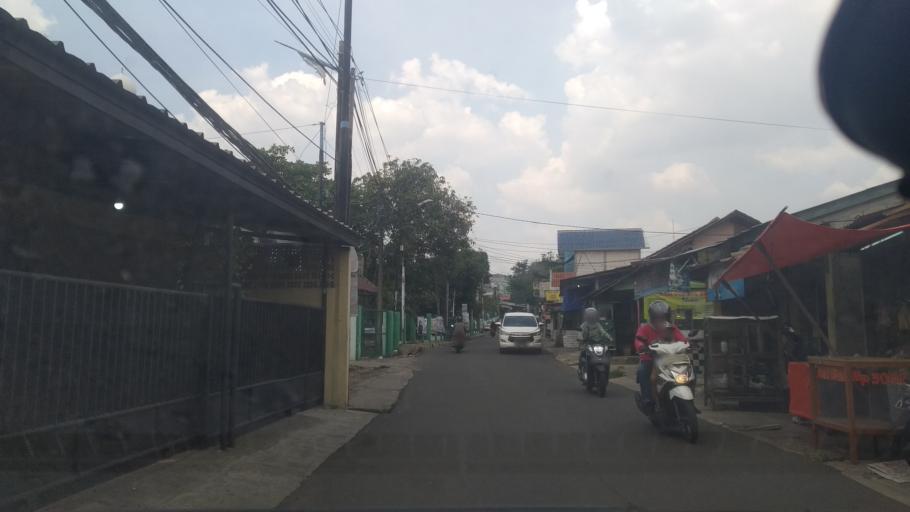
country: ID
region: Banten
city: South Tangerang
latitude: -6.2675
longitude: 106.7415
